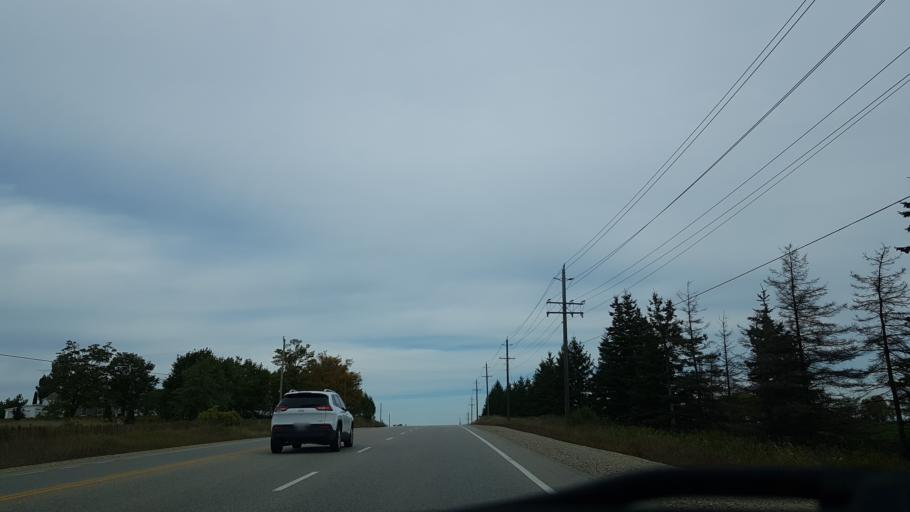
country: CA
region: Ontario
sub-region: Wellington County
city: Guelph
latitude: 43.6588
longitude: -80.1760
